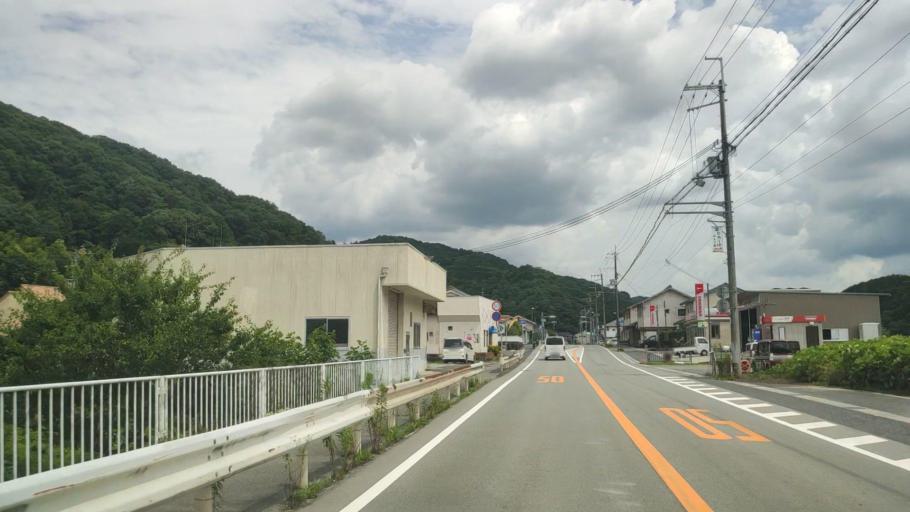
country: JP
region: Hyogo
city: Yamazakicho-nakabirose
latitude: 34.9858
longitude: 134.4345
